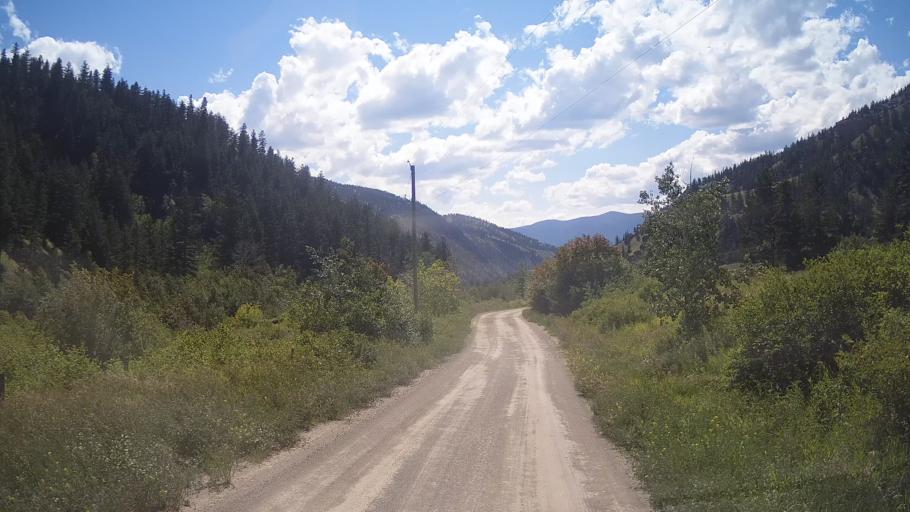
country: CA
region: British Columbia
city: Lillooet
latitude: 51.2399
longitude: -122.0433
